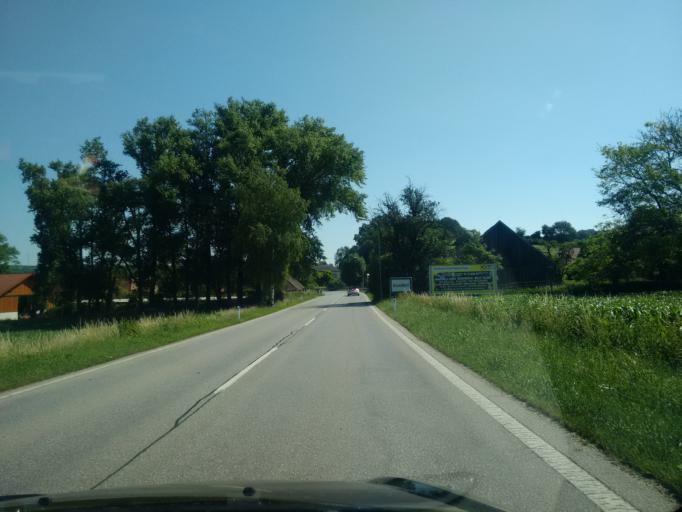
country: AT
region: Lower Austria
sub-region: Politischer Bezirk Tulln
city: Wurmla
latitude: 48.2634
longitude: 15.8175
